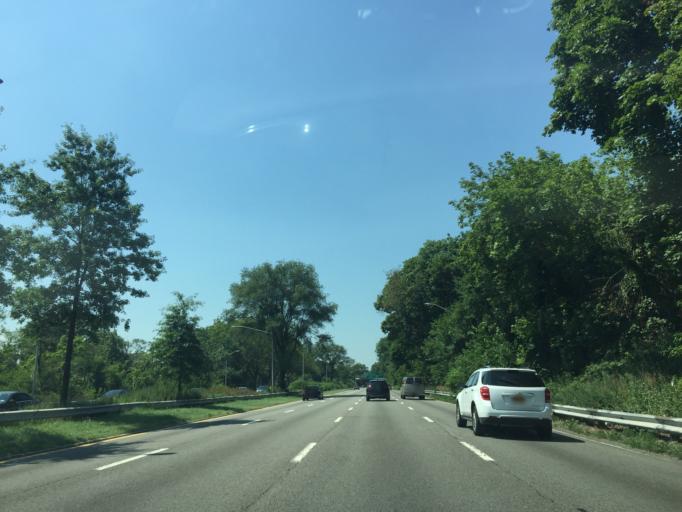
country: US
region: New York
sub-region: Nassau County
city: South Valley Stream
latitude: 40.6721
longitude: -73.7359
